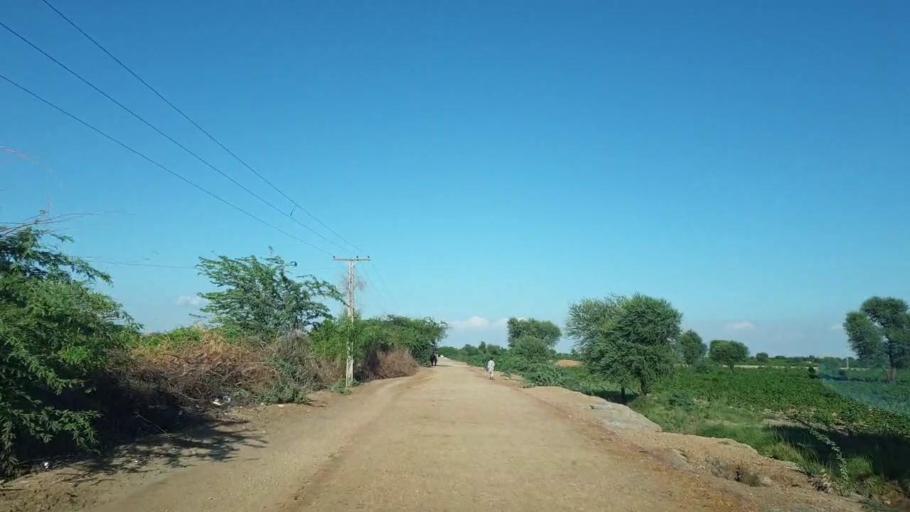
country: PK
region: Sindh
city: Dhoro Naro
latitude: 25.6395
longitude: 69.4928
